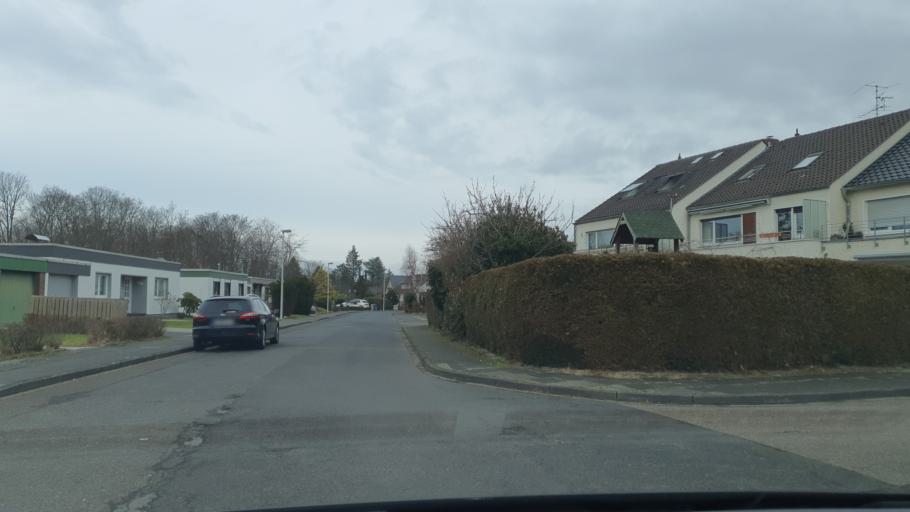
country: DE
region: North Rhine-Westphalia
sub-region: Regierungsbezirk Koln
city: Wachtberg
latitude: 50.6754
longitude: 7.0670
